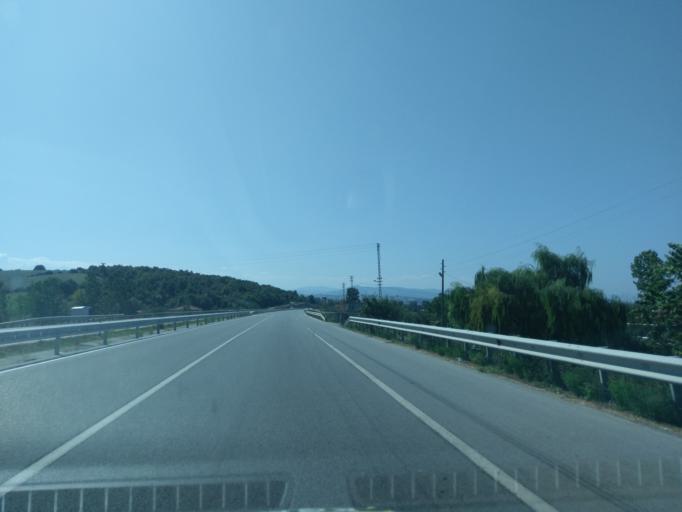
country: TR
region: Samsun
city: Alacam
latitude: 41.6097
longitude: 35.6945
